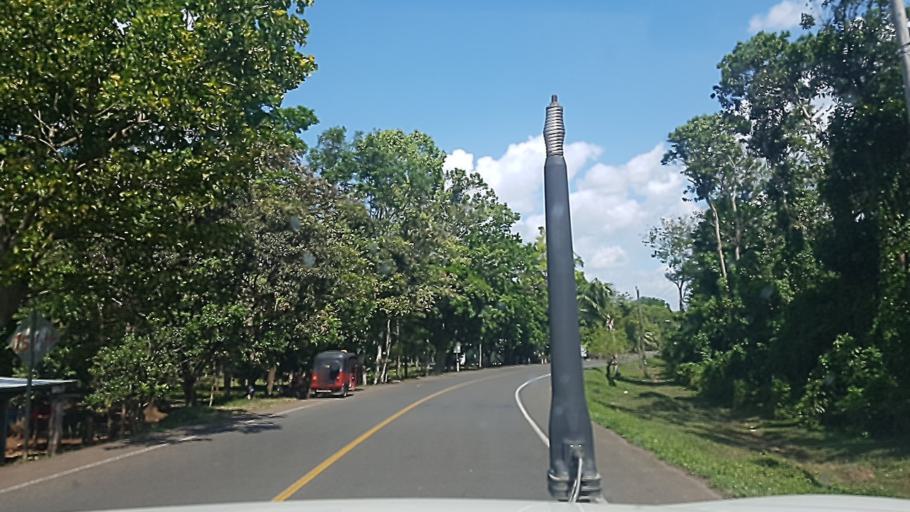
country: NI
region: Atlantico Sur
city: Muelle de los Bueyes
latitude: 11.9125
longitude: -84.6418
